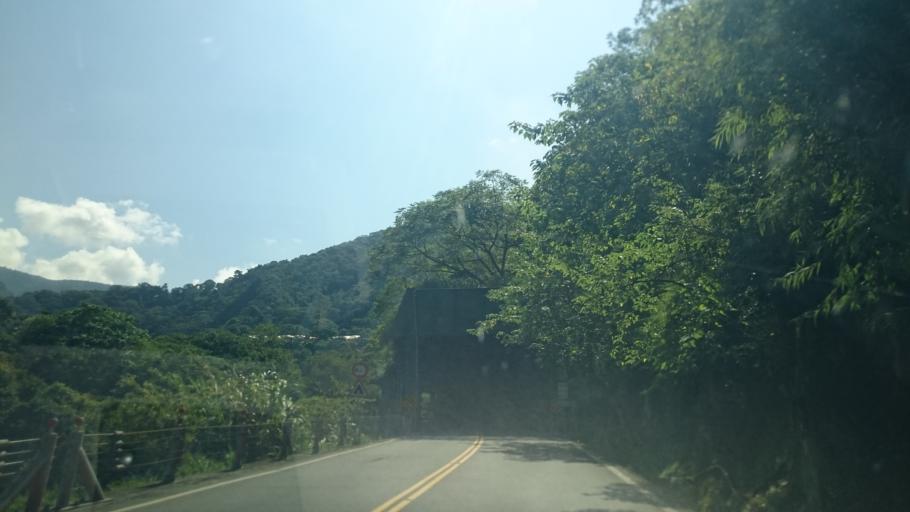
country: TW
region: Taiwan
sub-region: Nantou
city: Puli
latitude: 23.9977
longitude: 121.0481
